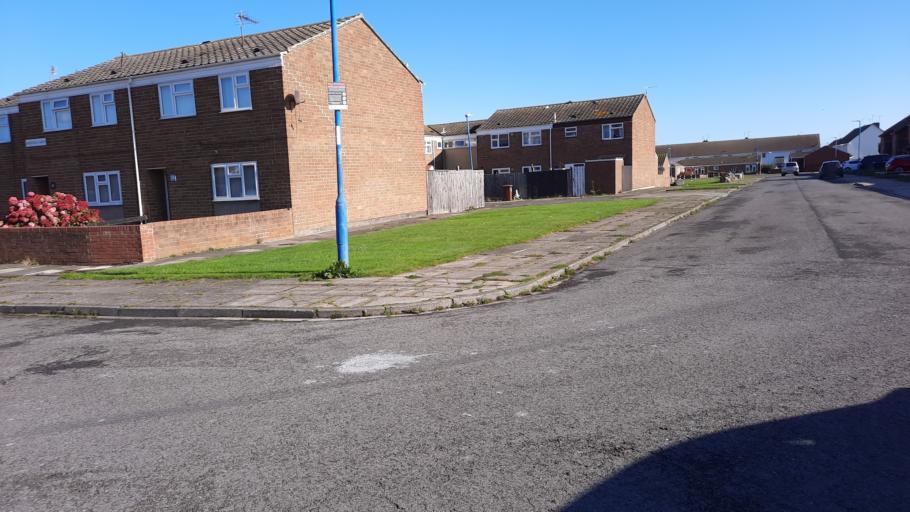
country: GB
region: England
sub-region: Hartlepool
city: Hartlepool
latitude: 54.6825
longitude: -1.2053
